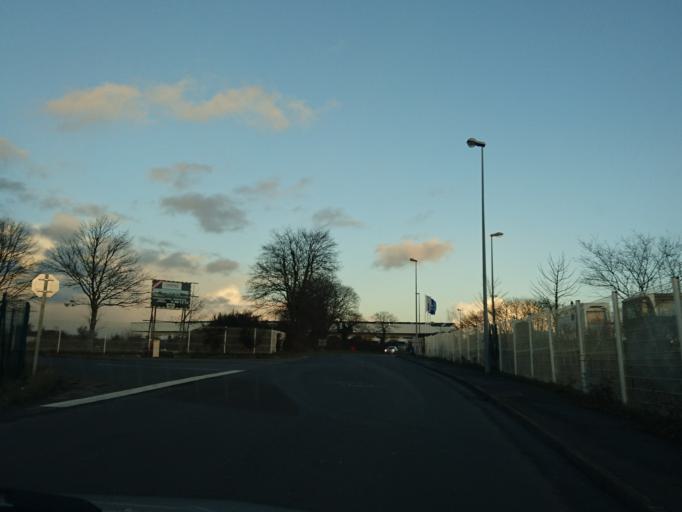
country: FR
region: Brittany
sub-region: Departement du Finistere
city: Gouesnou
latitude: 48.4317
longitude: -4.4461
